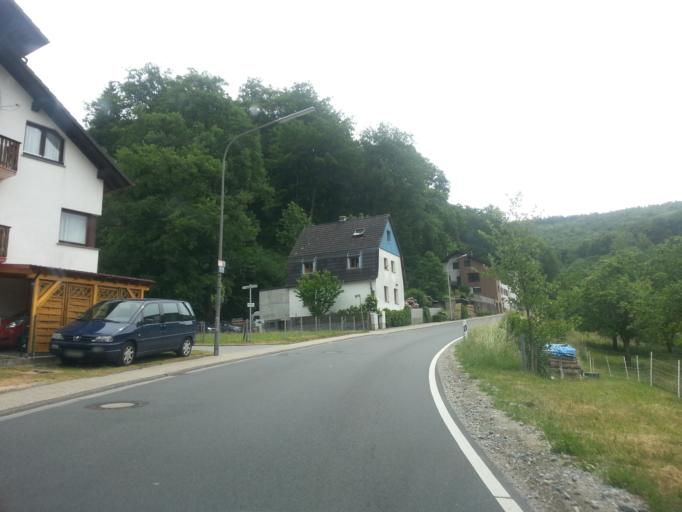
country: DE
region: Hesse
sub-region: Regierungsbezirk Darmstadt
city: Seeheim-Jugenheim
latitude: 49.7316
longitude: 8.6646
